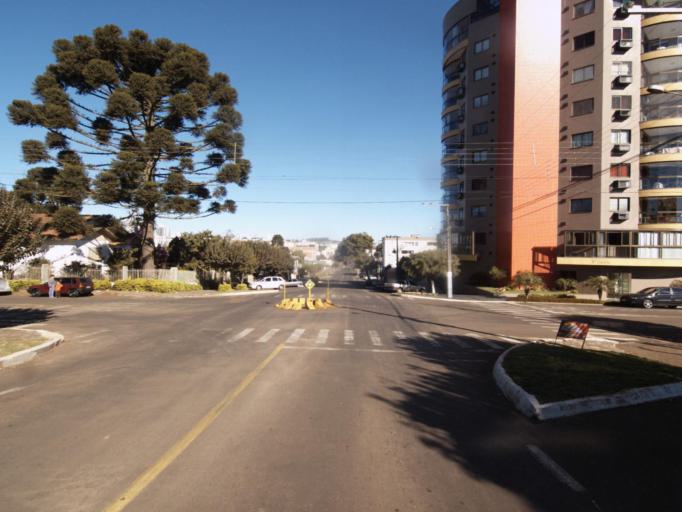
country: AR
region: Misiones
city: Bernardo de Irigoyen
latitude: -26.7248
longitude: -53.5218
